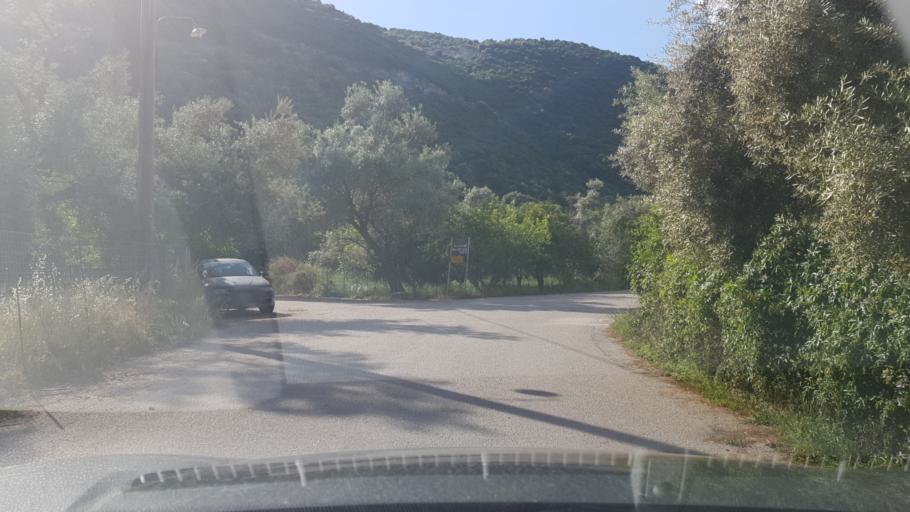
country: GR
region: Ionian Islands
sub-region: Lefkada
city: Nidri
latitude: 38.7161
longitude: 20.6959
